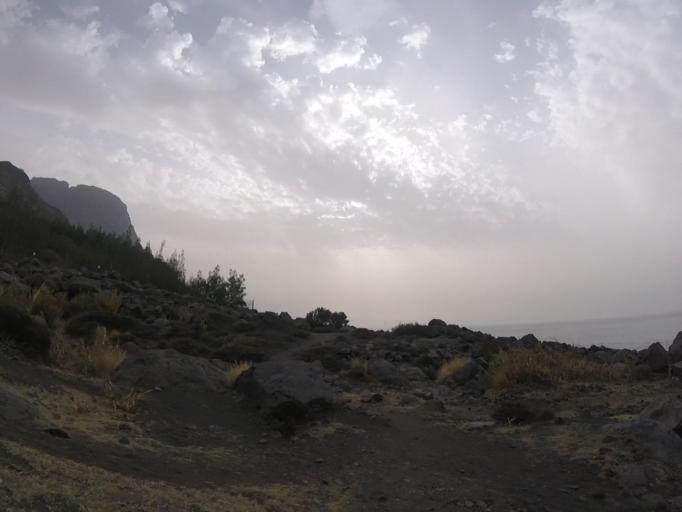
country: ES
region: Canary Islands
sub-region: Provincia de Las Palmas
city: Agaete
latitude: 28.0866
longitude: -15.7094
